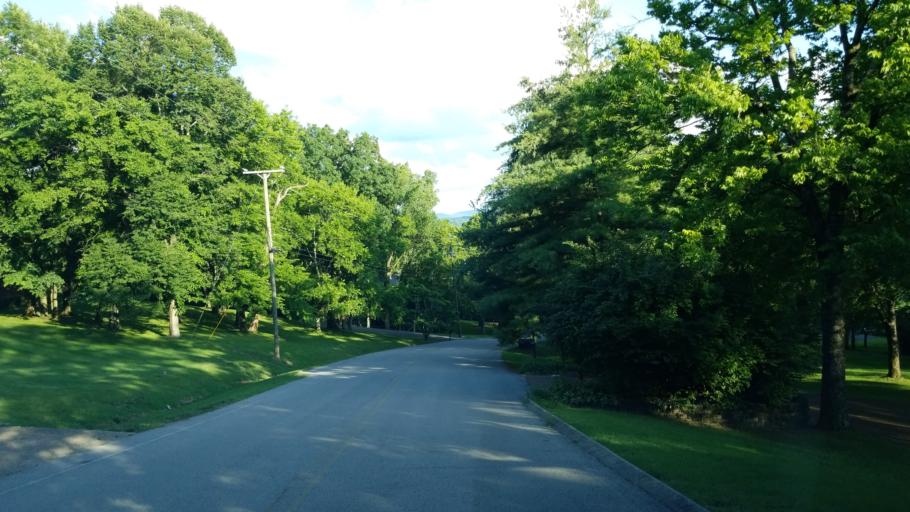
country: US
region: Tennessee
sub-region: Williamson County
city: Brentwood
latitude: 36.0403
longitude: -86.7912
